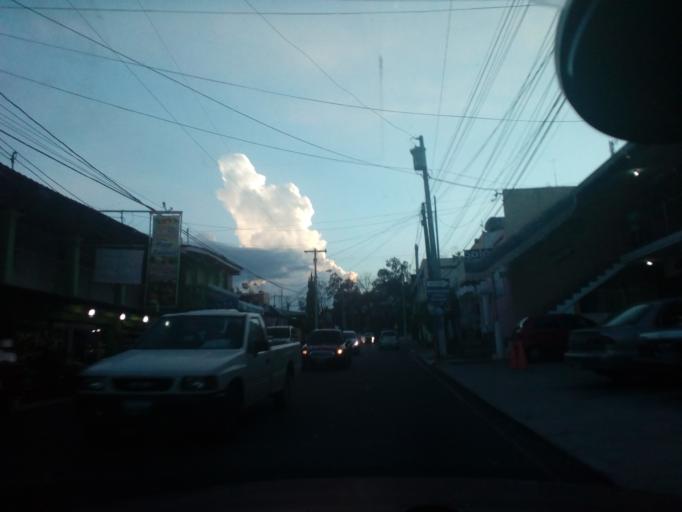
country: GT
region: Guatemala
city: Mixco
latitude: 14.6035
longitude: -90.5813
